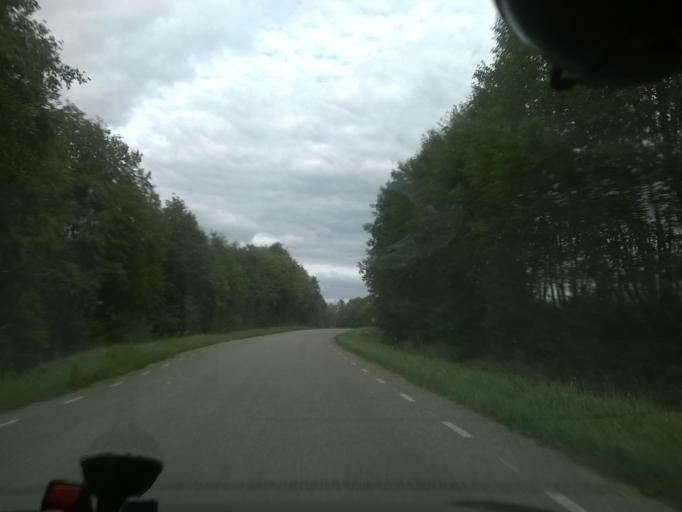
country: EE
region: Vorumaa
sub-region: Voru linn
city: Voru
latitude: 57.7663
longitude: 27.0147
